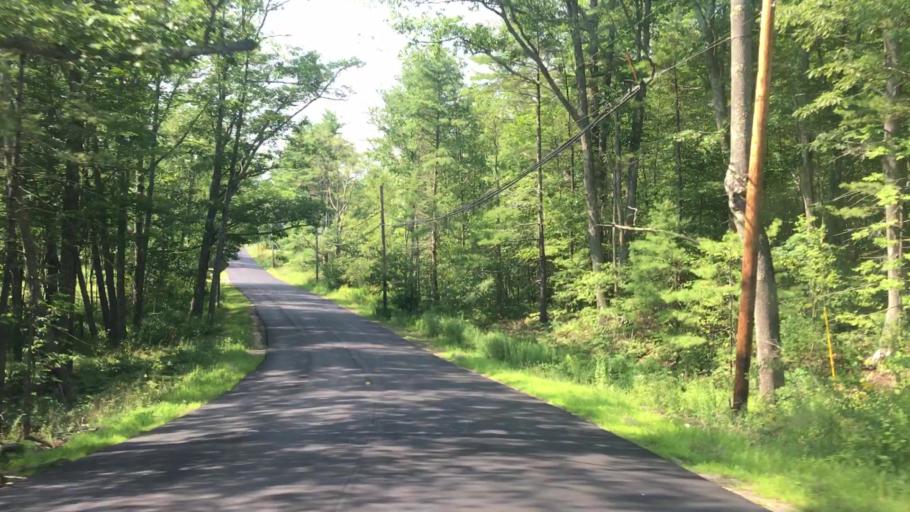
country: US
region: Maine
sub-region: Sagadahoc County
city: North Bath
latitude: 43.9455
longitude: -69.8051
